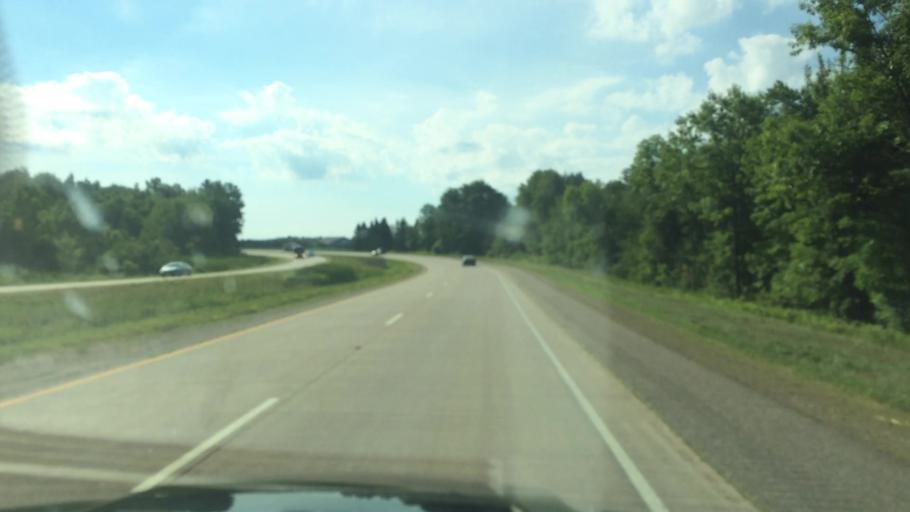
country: US
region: Wisconsin
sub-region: Shawano County
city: Wittenberg
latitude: 44.8059
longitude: -89.0350
